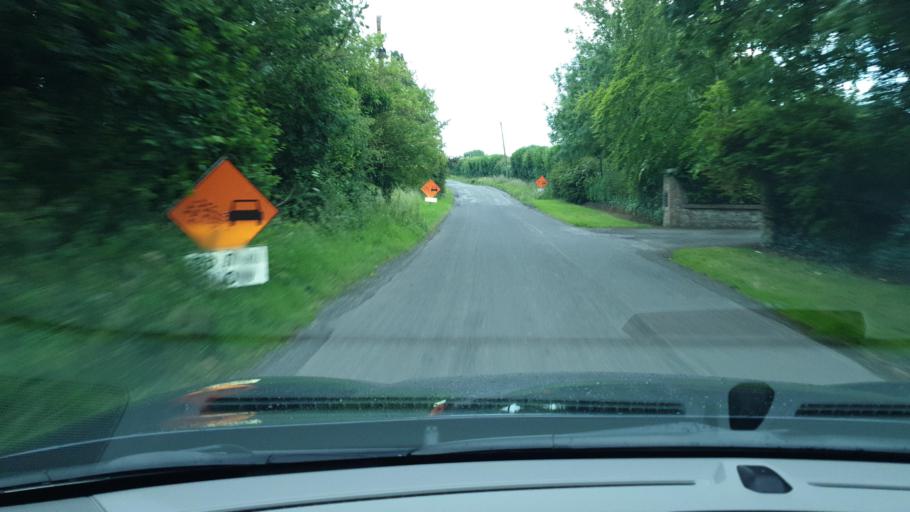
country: IE
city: Kentstown
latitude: 53.5927
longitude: -6.5736
